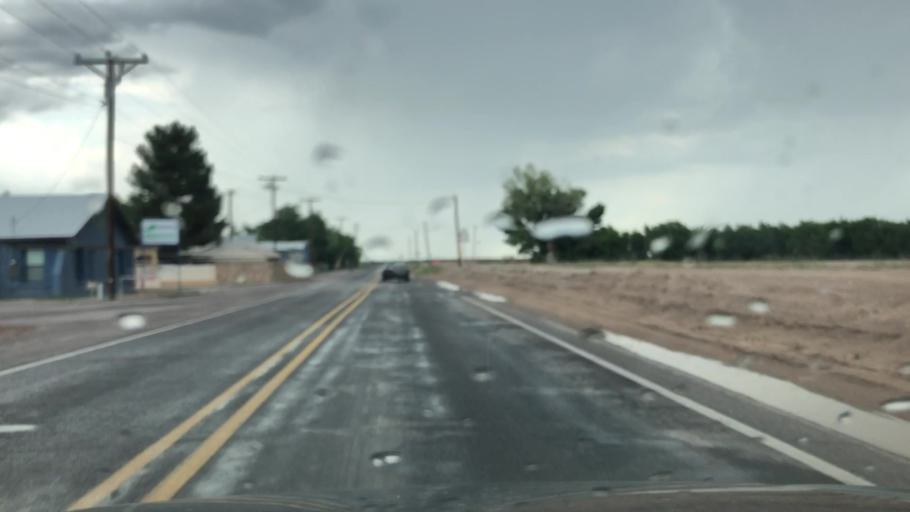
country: US
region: New Mexico
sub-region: Dona Ana County
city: Vado
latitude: 32.0595
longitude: -106.6767
